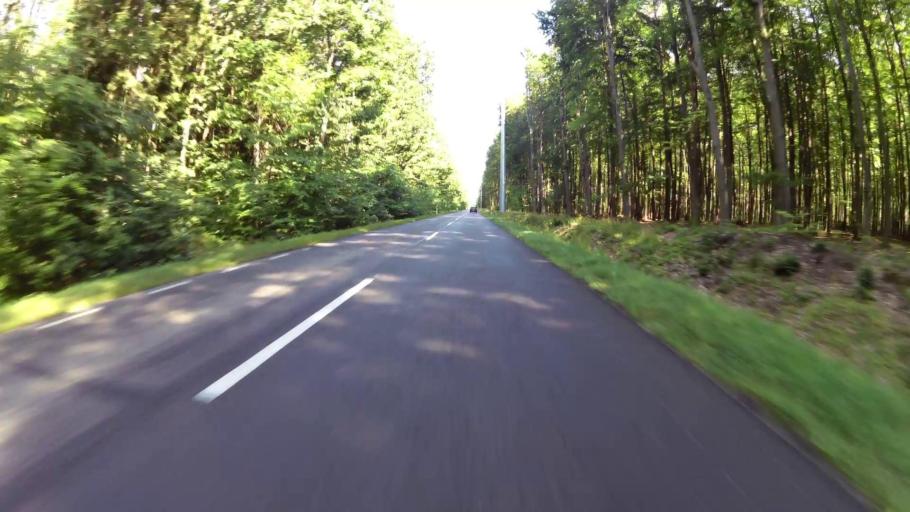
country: PL
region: West Pomeranian Voivodeship
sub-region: Powiat drawski
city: Czaplinek
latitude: 53.4516
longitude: 16.2143
